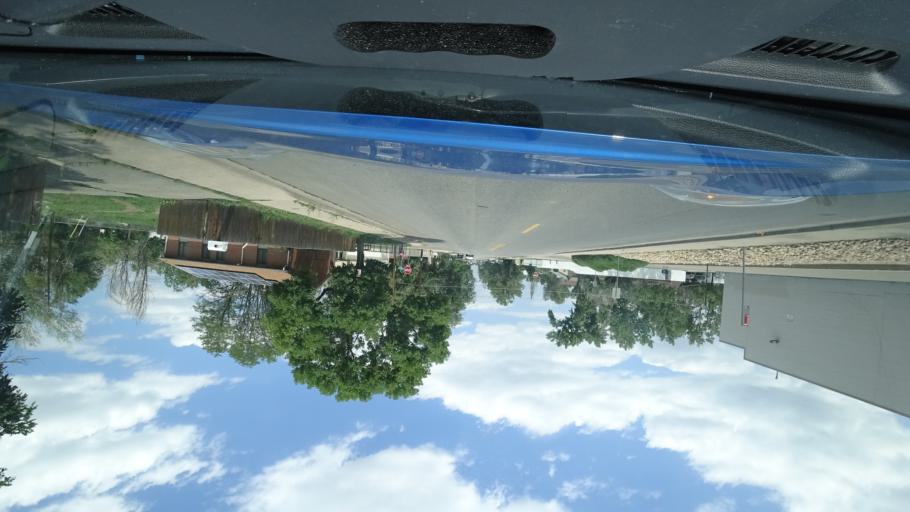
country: US
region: Colorado
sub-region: Arapahoe County
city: Sheridan
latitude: 39.6801
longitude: -105.0203
